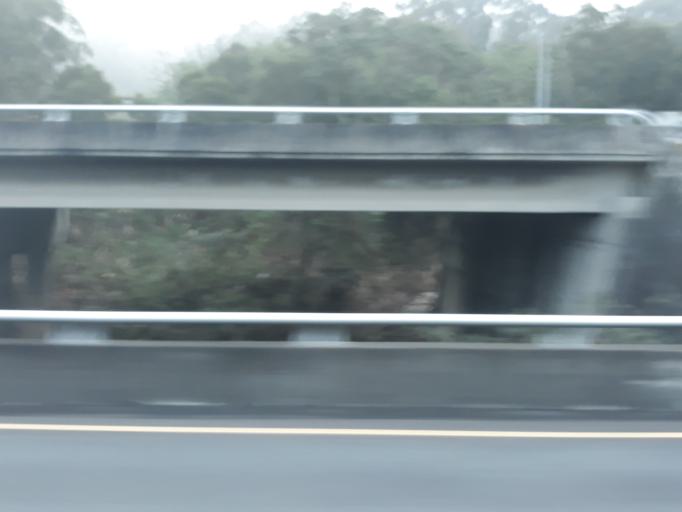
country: TW
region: Taiwan
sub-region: Miaoli
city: Miaoli
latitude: 24.4412
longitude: 120.7797
